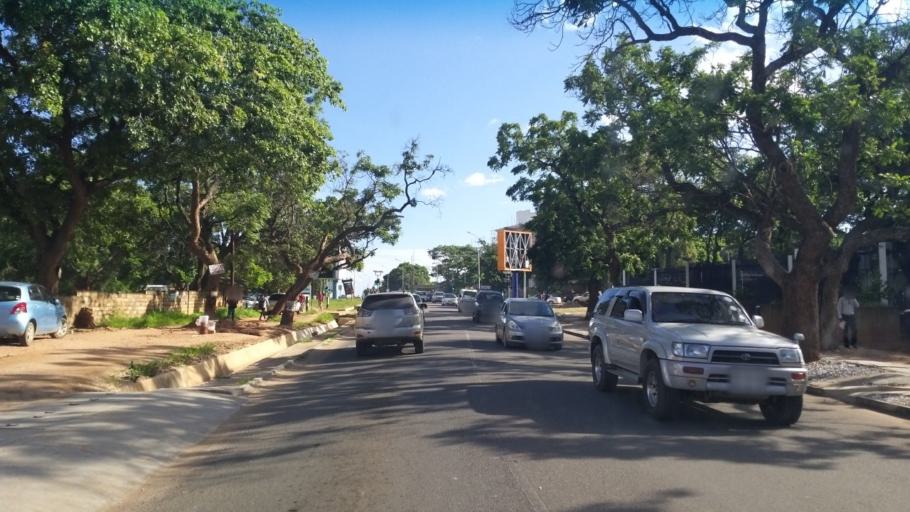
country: ZM
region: Lusaka
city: Lusaka
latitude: -15.4240
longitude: 28.3120
